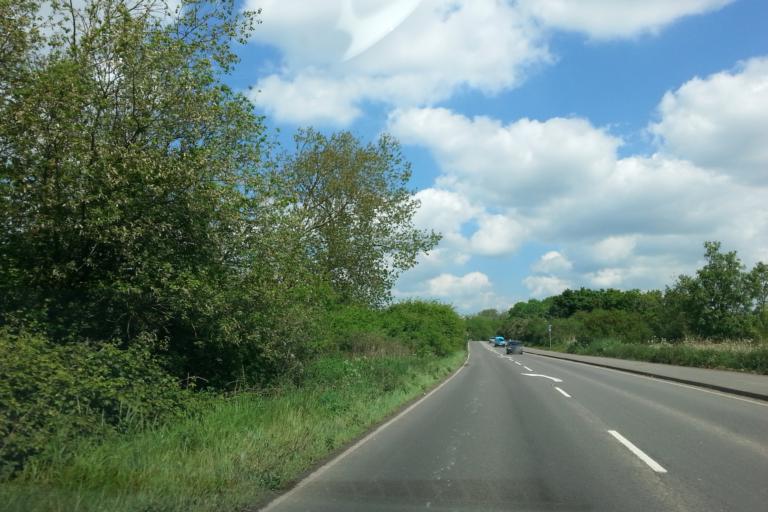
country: GB
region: England
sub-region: Cambridgeshire
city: Yaxley
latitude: 52.5236
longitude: -0.2687
